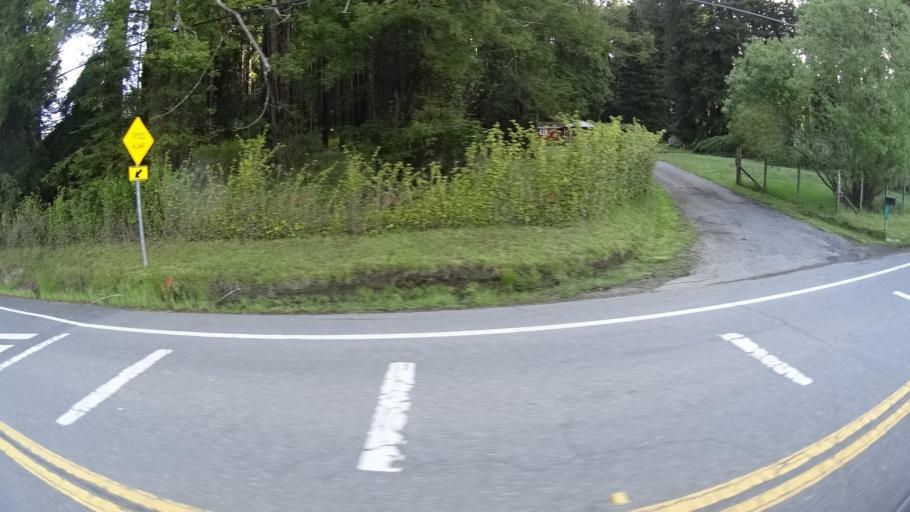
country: US
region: California
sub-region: Humboldt County
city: Myrtletown
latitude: 40.7606
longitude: -124.0589
